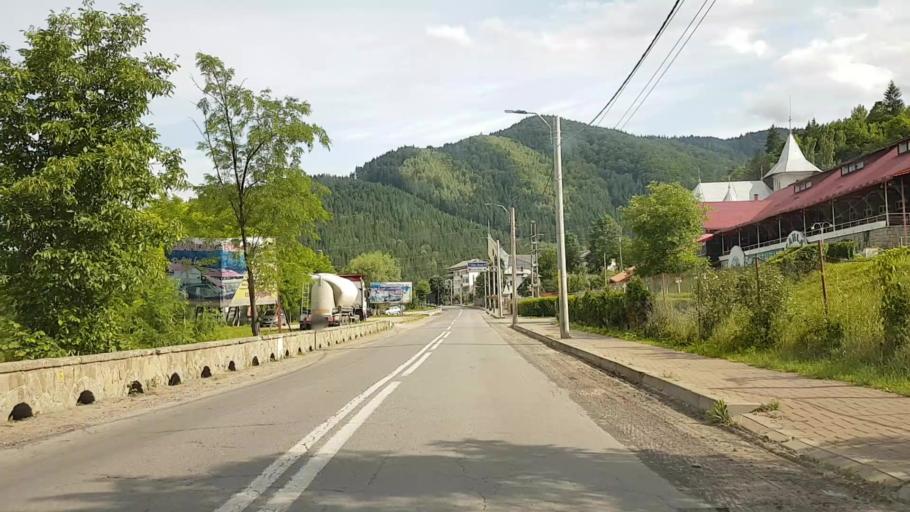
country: RO
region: Neamt
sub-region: Comuna Bicaz
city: Dodeni
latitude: 46.9159
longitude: 26.0857
